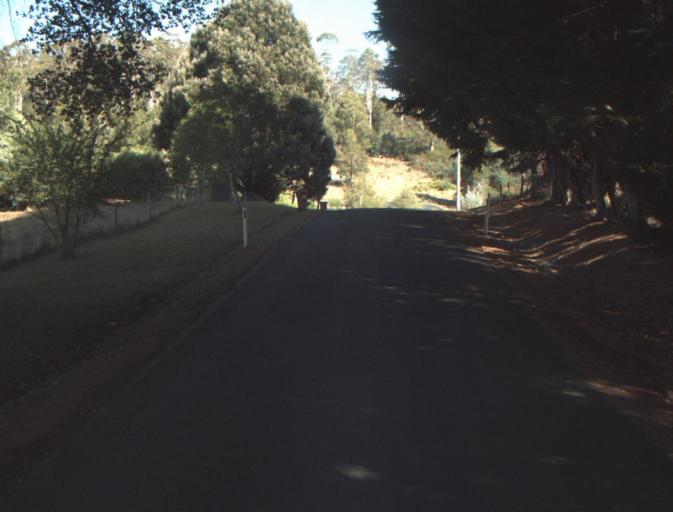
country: AU
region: Tasmania
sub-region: Launceston
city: Mayfield
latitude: -41.2935
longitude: 147.2041
